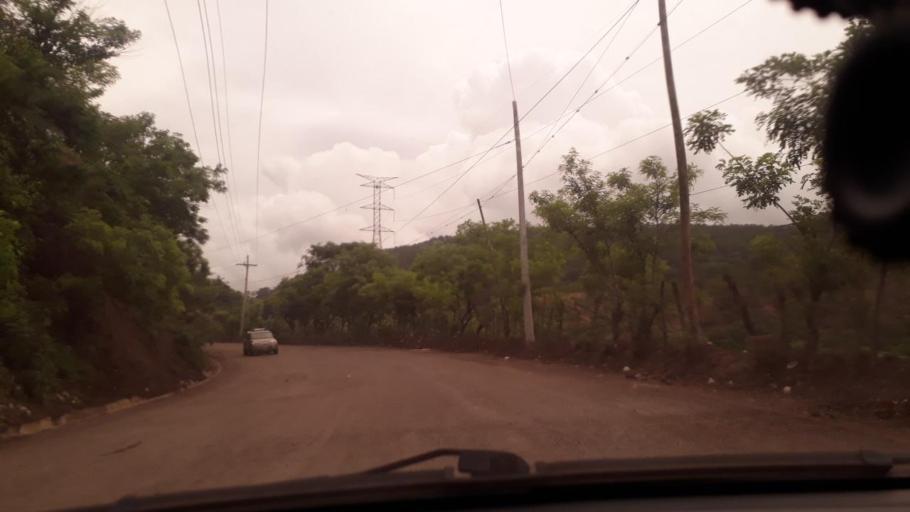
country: GT
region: Chiquimula
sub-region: Municipio de San Juan Ermita
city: San Juan Ermita
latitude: 14.7553
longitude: -89.4429
